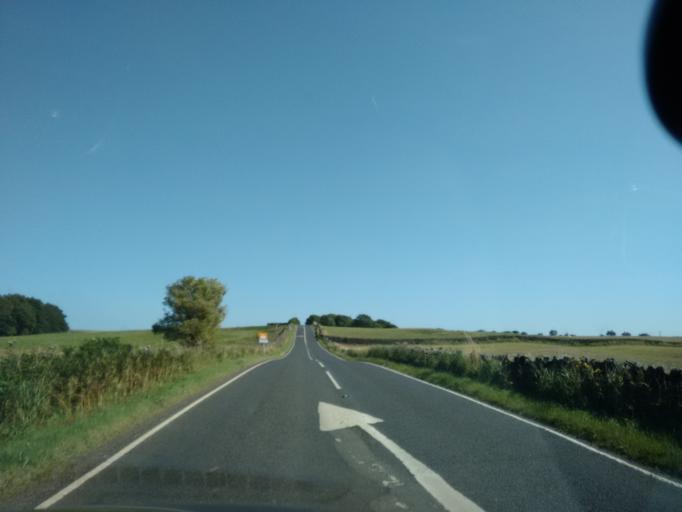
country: GB
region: England
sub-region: Northumberland
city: Acomb
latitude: 55.0185
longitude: -2.0673
